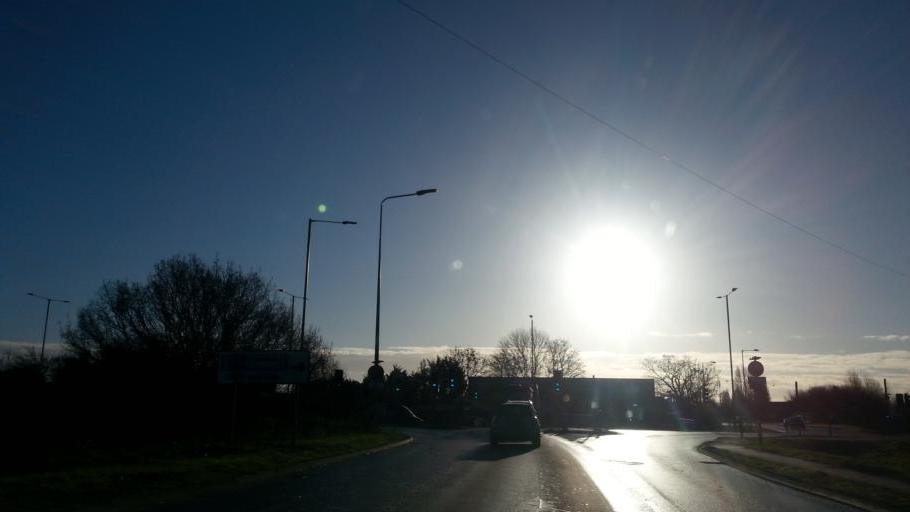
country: GB
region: England
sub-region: Suffolk
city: Bramford
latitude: 52.0470
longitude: 1.1066
